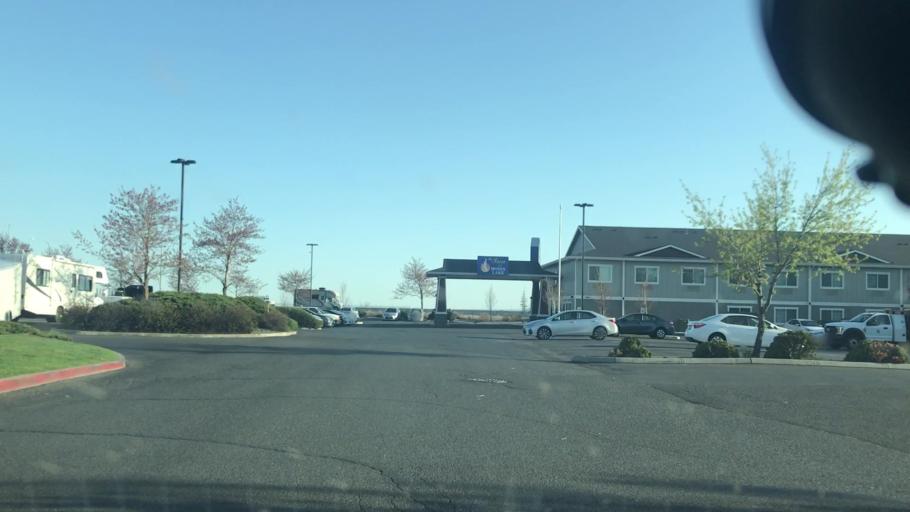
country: US
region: Washington
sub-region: Grant County
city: Moses Lake
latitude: 47.1006
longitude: -119.2479
